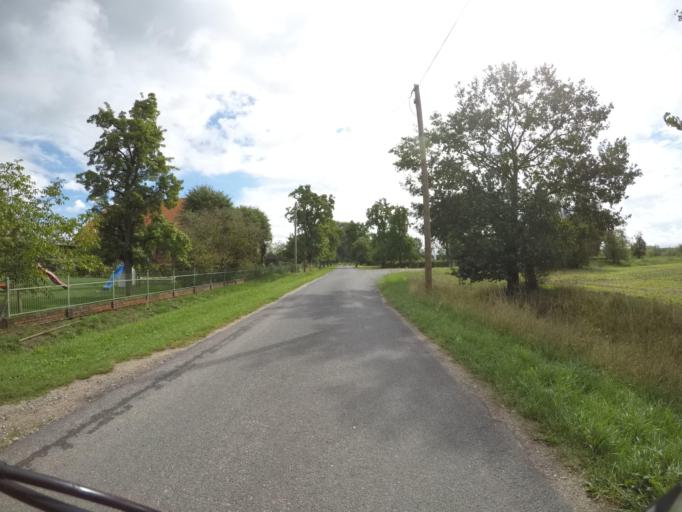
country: DE
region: Lower Saxony
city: Neu Darchau
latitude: 53.2585
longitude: 10.8596
